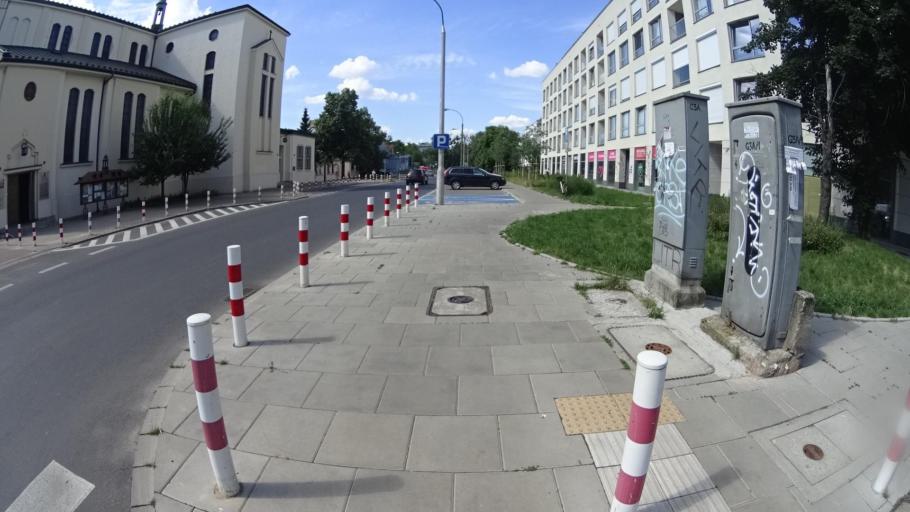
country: PL
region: Masovian Voivodeship
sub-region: Warszawa
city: Wola
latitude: 52.2340
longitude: 20.9769
